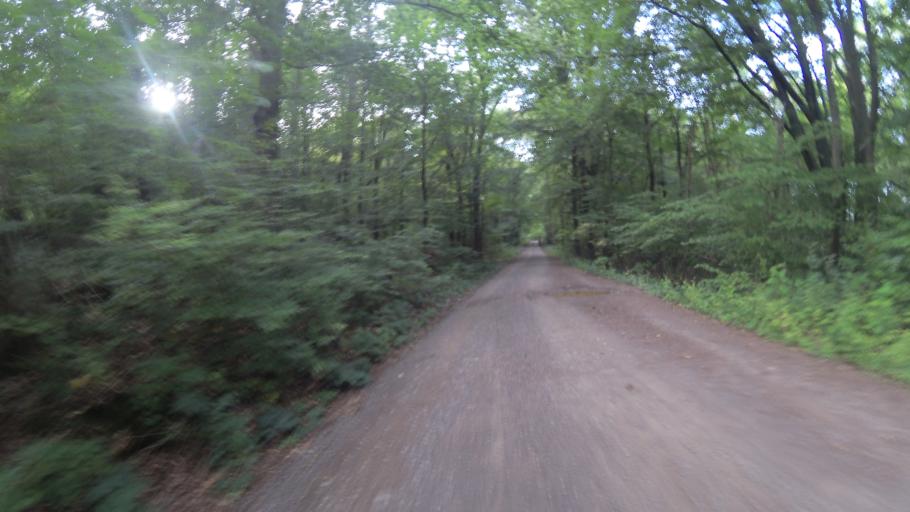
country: DE
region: Saarland
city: Namborn
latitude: 49.5383
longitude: 7.1341
